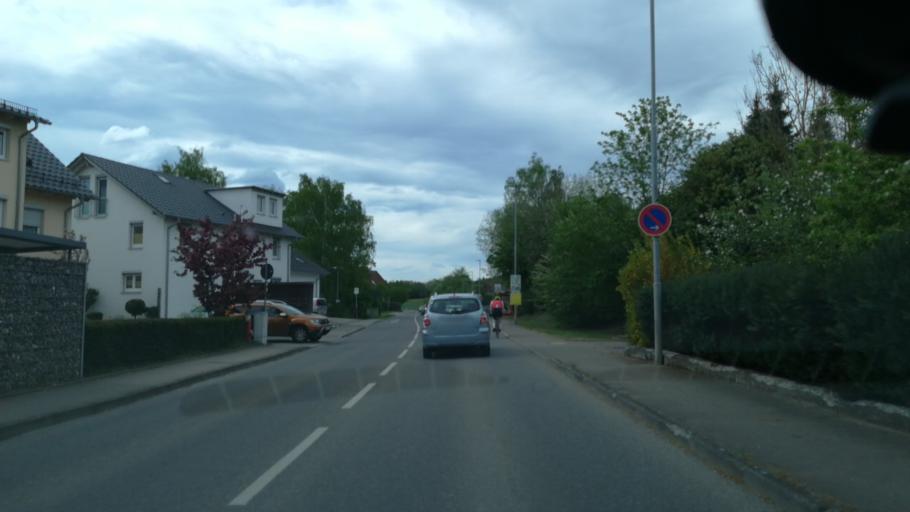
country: DE
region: Baden-Wuerttemberg
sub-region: Freiburg Region
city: Radolfzell am Bodensee
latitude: 47.7440
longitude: 9.0010
